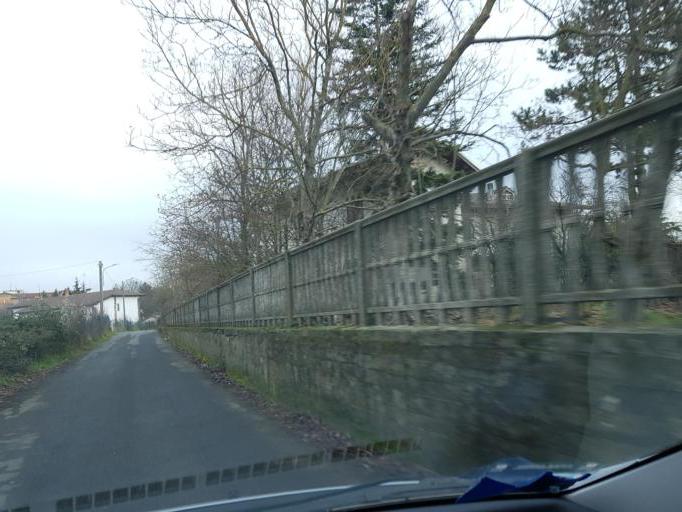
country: IT
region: Piedmont
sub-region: Provincia di Alessandria
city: Novi Ligure
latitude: 44.7698
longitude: 8.7977
